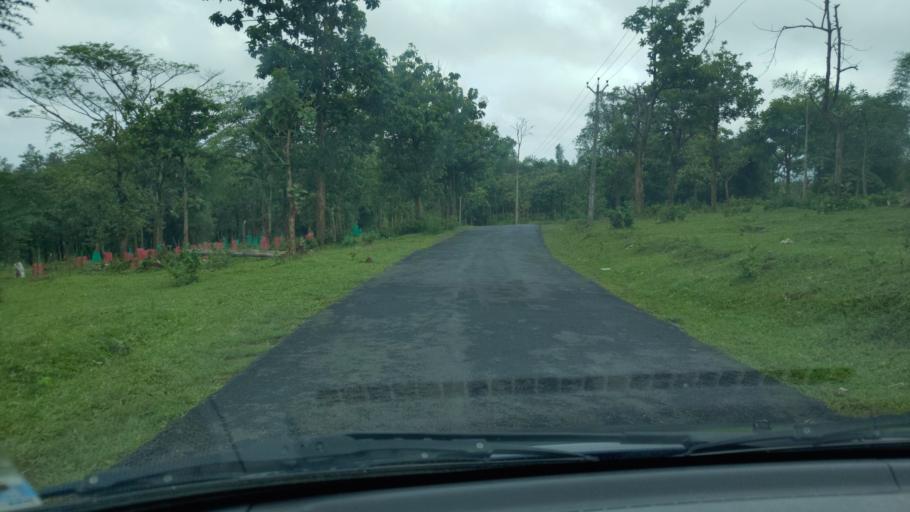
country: IN
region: Kerala
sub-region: Wayanad
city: Panamaram
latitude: 11.7082
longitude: 76.2758
